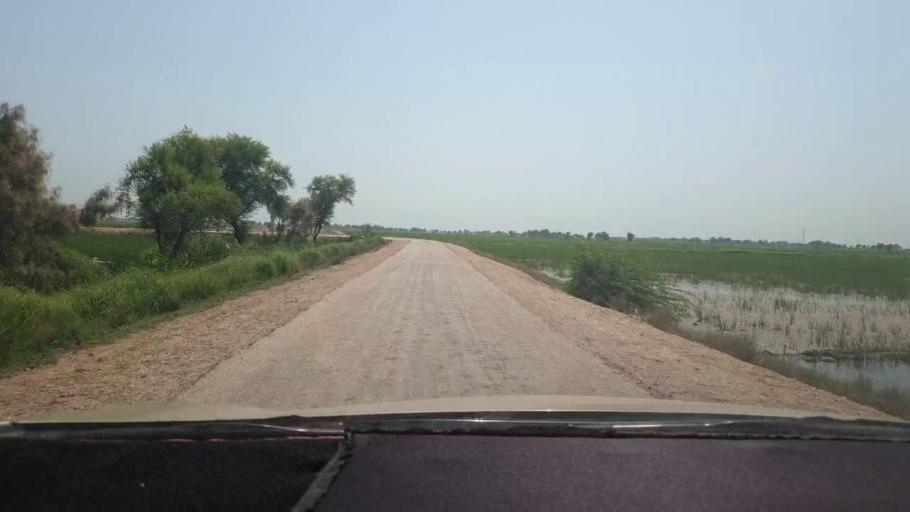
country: PK
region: Sindh
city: Miro Khan
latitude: 27.6755
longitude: 68.0944
